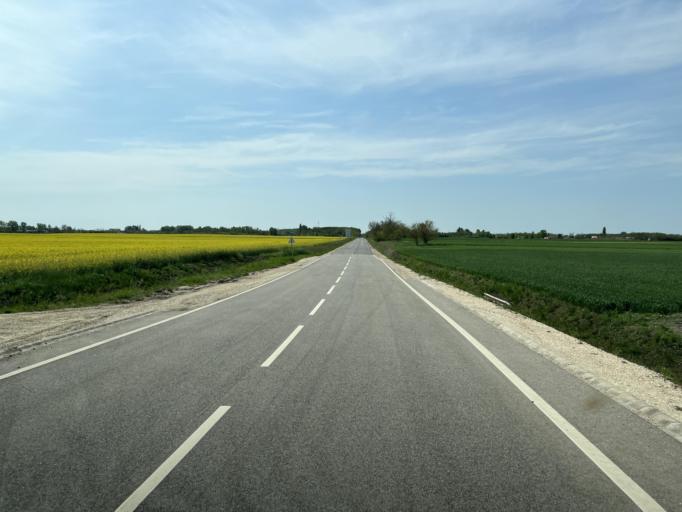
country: HU
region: Pest
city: Abony
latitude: 47.2178
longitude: 20.0167
